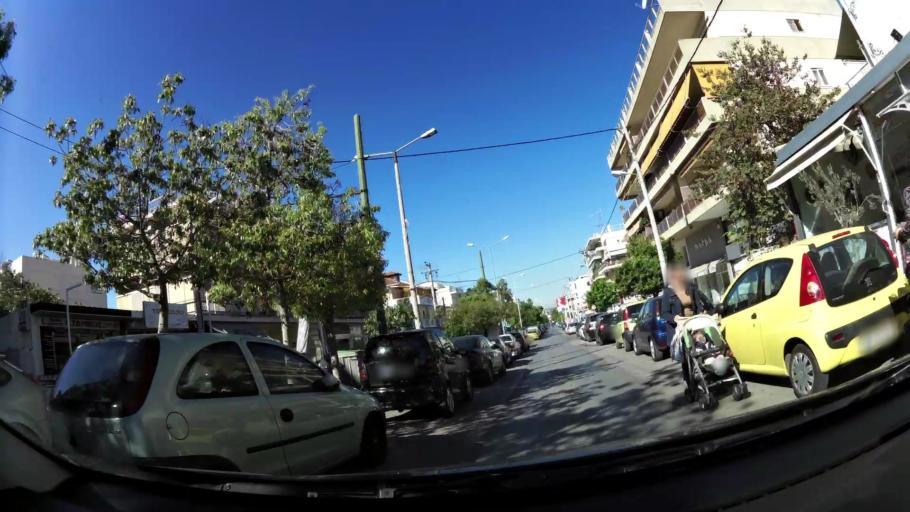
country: GR
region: Attica
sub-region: Nomarchia Athinas
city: Khalandrion
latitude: 38.0222
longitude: 23.7964
